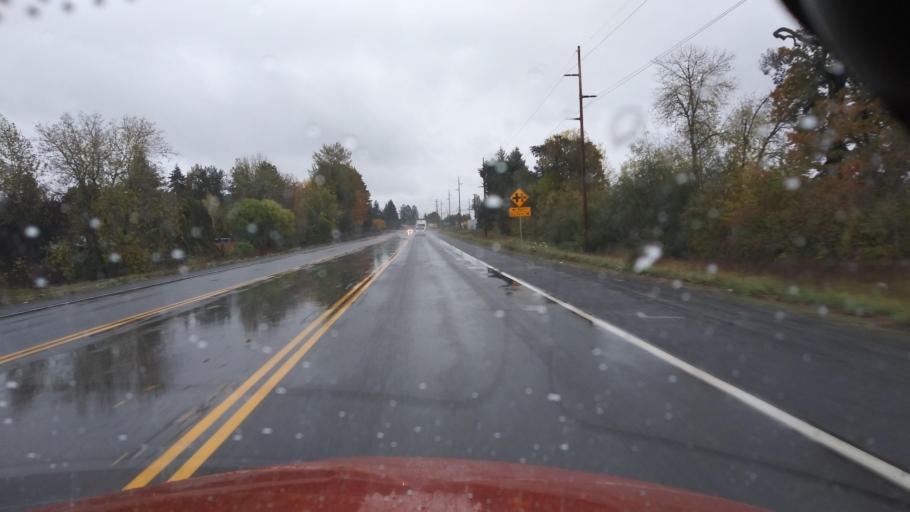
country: US
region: Oregon
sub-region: Washington County
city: Forest Grove
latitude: 45.5110
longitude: -123.0948
